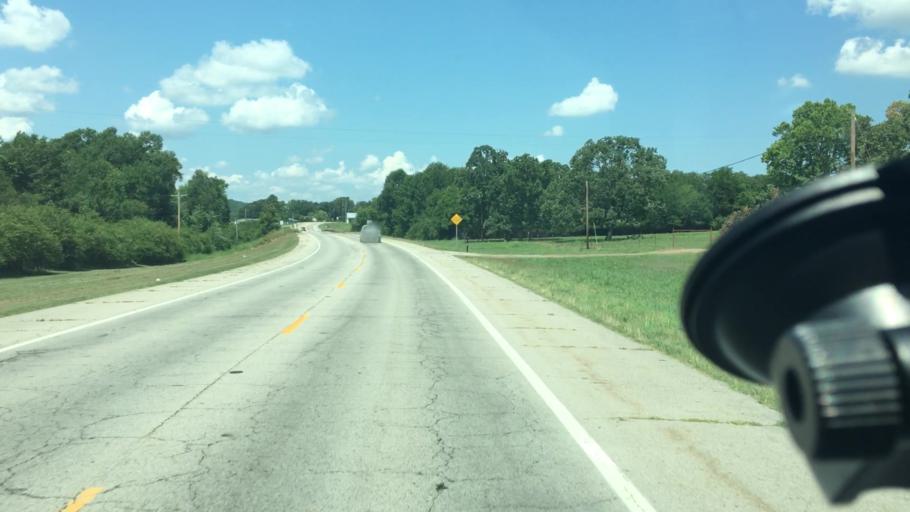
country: US
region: Arkansas
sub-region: Sebastian County
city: Lavaca
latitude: 35.2927
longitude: -94.1300
